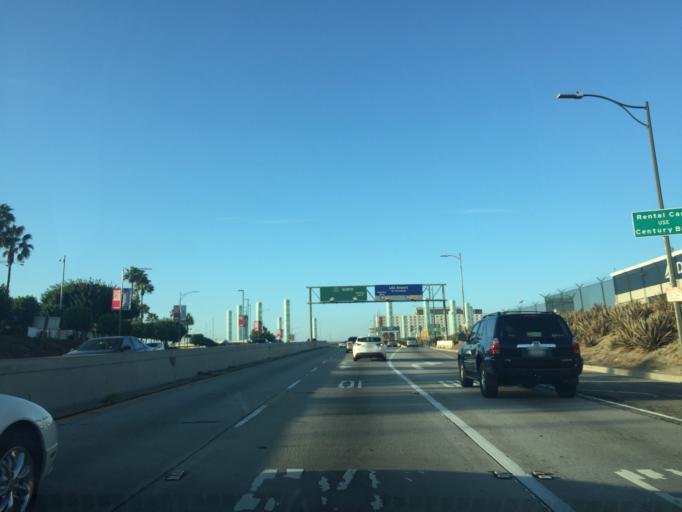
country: US
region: California
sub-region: Los Angeles County
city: El Segundo
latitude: 33.9406
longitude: -118.3961
